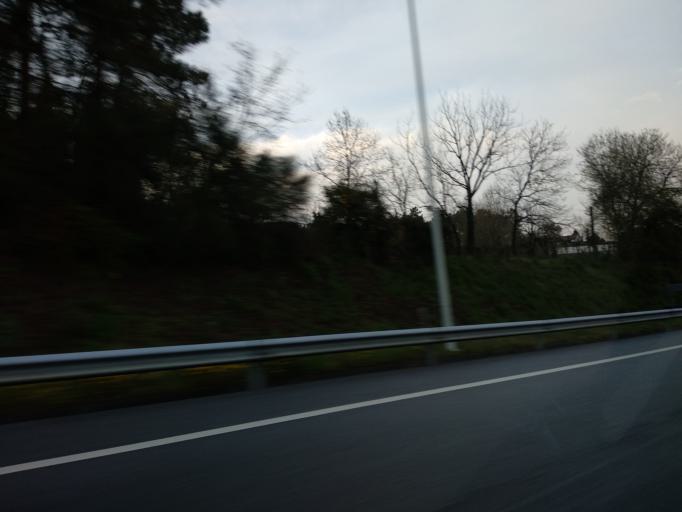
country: PT
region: Braga
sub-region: Braga
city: Oliveira
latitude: 41.5080
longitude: -8.4656
